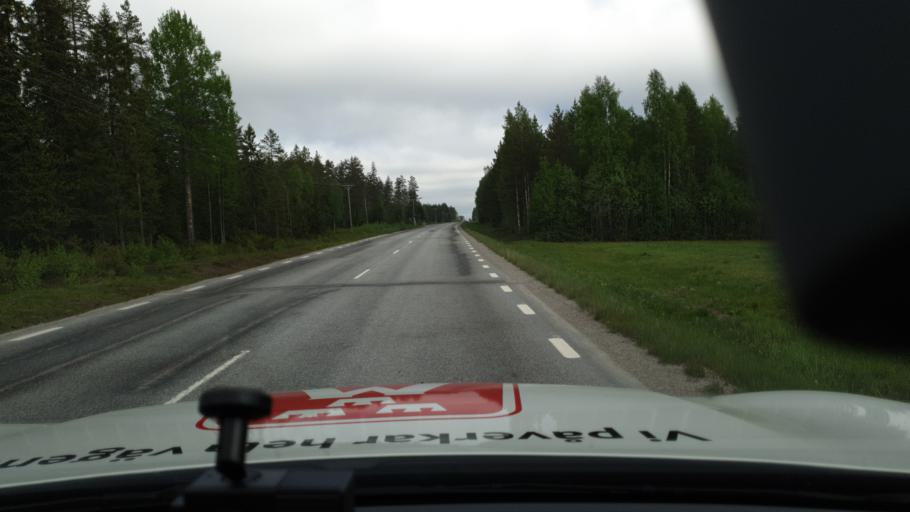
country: SE
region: Vaesterbotten
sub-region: Umea Kommun
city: Roback
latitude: 63.8947
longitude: 20.1977
